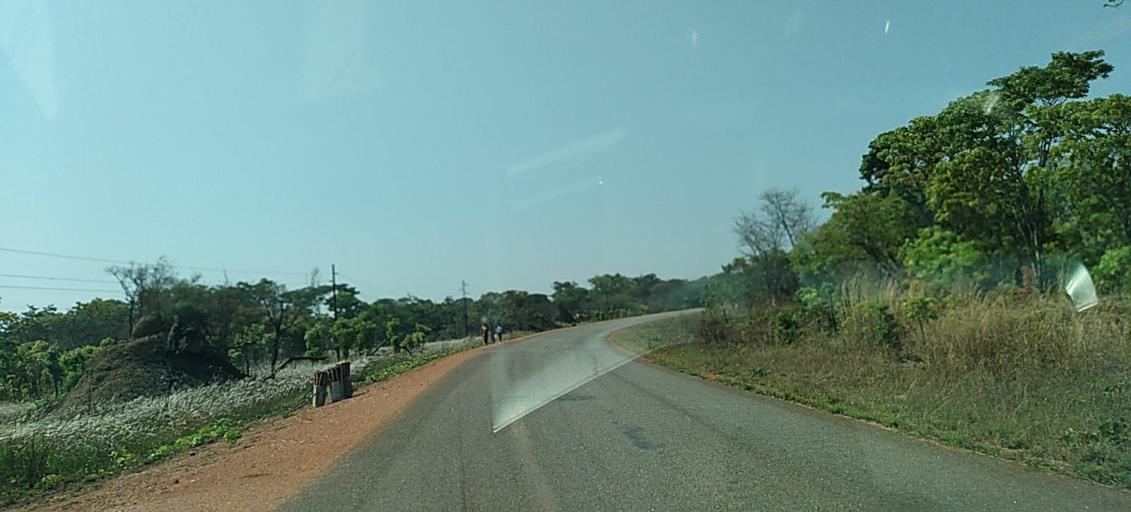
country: ZM
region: North-Western
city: Solwezi
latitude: -12.1453
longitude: 25.5404
